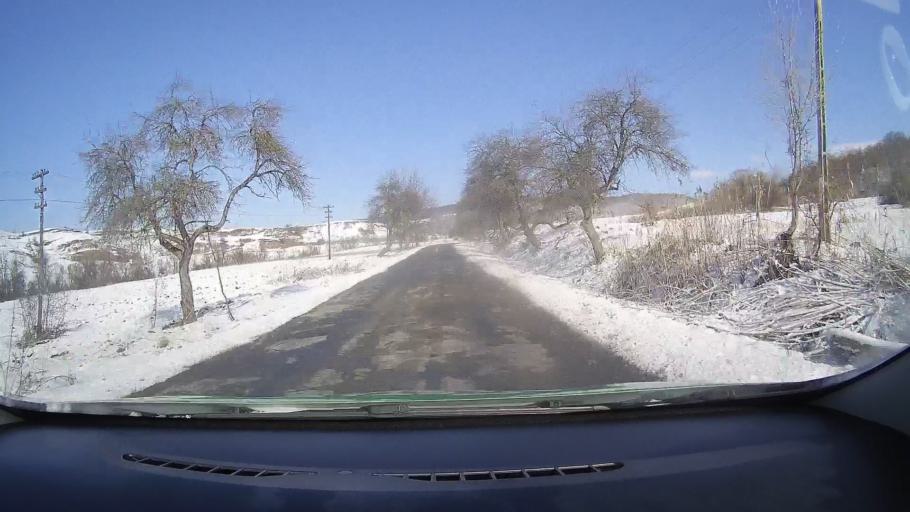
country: RO
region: Sibiu
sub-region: Comuna Mihaileni
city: Mihaileni
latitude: 46.0183
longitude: 24.3873
